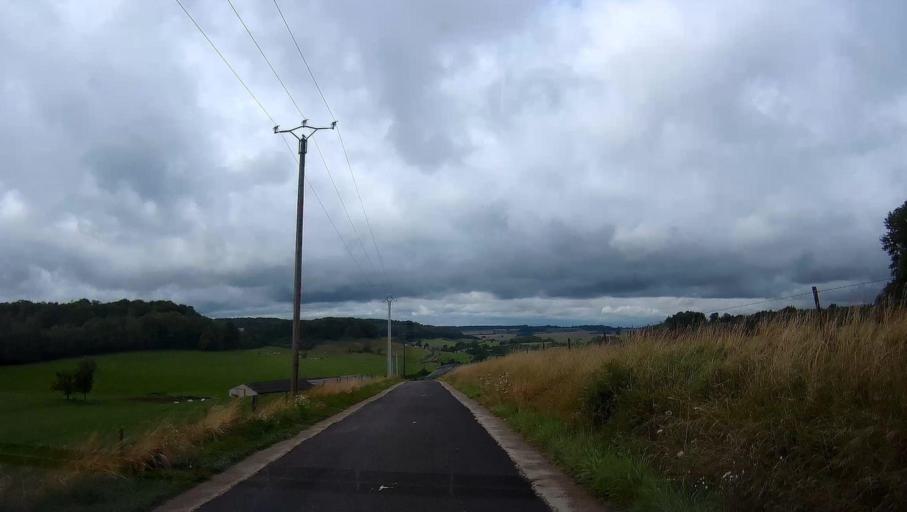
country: FR
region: Champagne-Ardenne
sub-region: Departement des Ardennes
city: Rimogne
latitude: 49.7661
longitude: 4.4953
